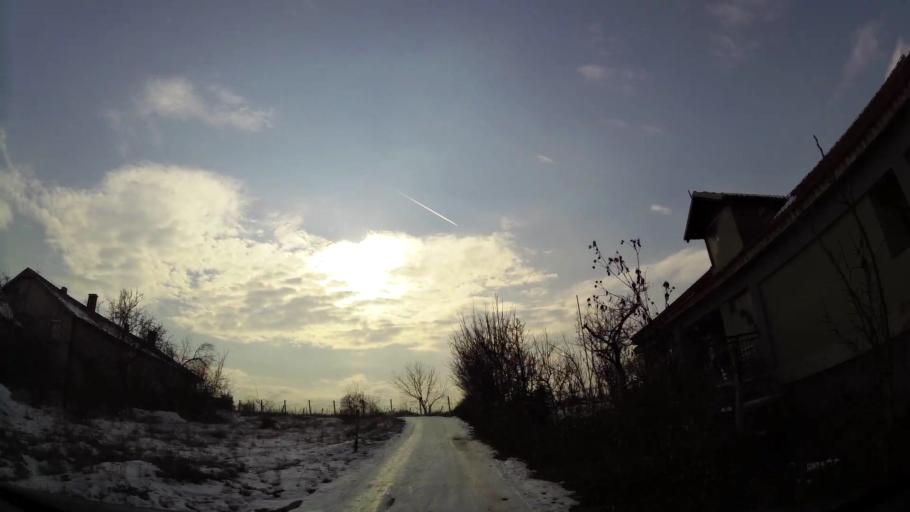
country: MK
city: Creshevo
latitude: 42.0105
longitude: 21.4956
